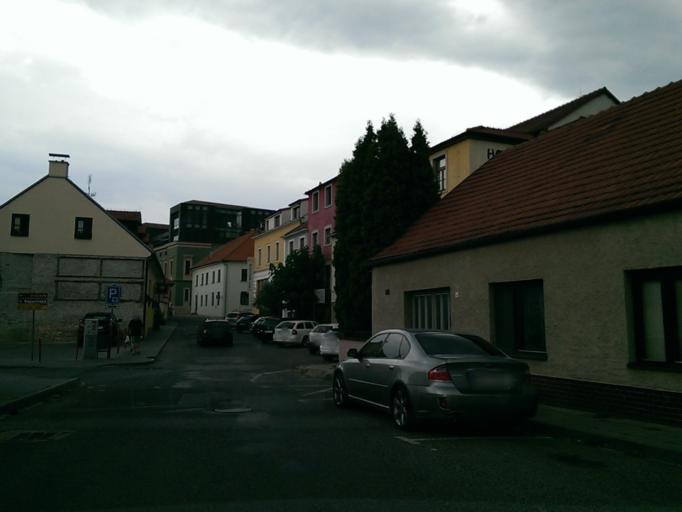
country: CZ
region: South Moravian
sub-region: Okres Breclav
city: Mikulov
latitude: 48.8070
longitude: 16.6412
